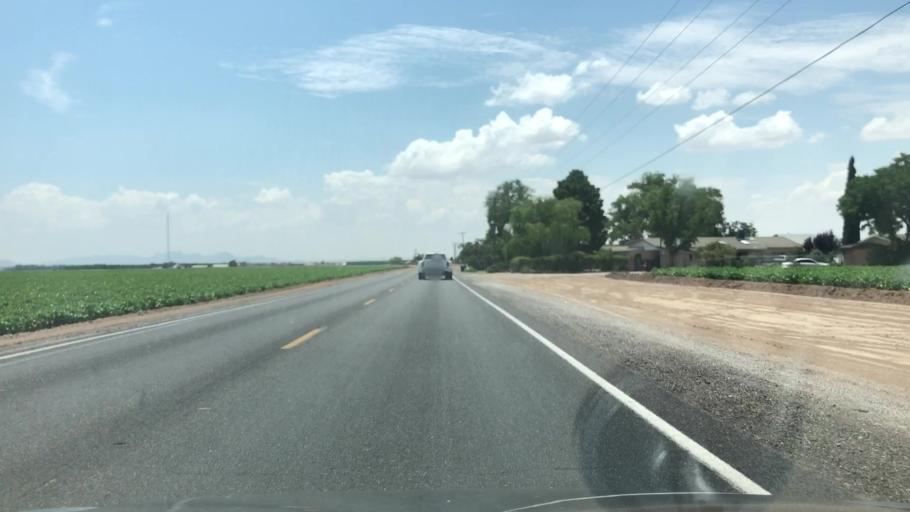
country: US
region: New Mexico
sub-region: Dona Ana County
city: La Union
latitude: 31.9784
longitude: -106.6515
